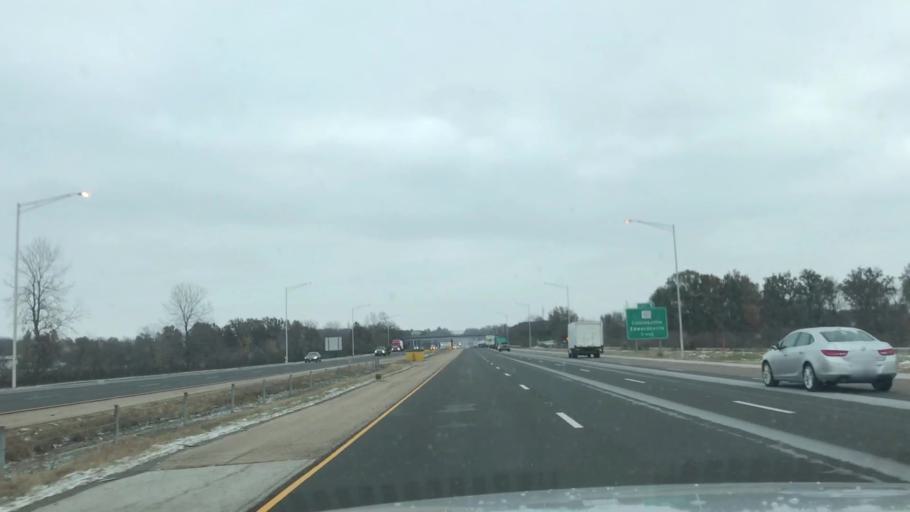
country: US
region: Illinois
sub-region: Madison County
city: Glen Carbon
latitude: 38.7569
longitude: -90.0305
